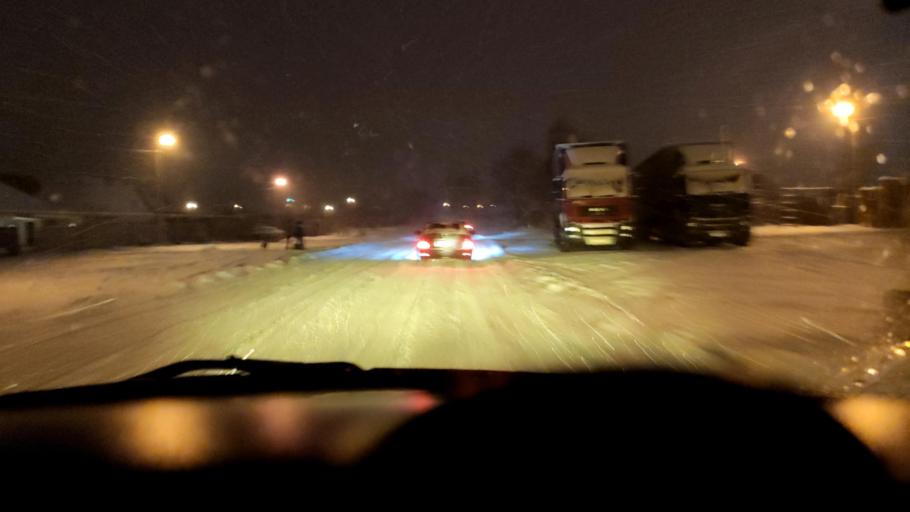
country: RU
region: Voronezj
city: Pridonskoy
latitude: 51.6710
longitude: 39.0793
